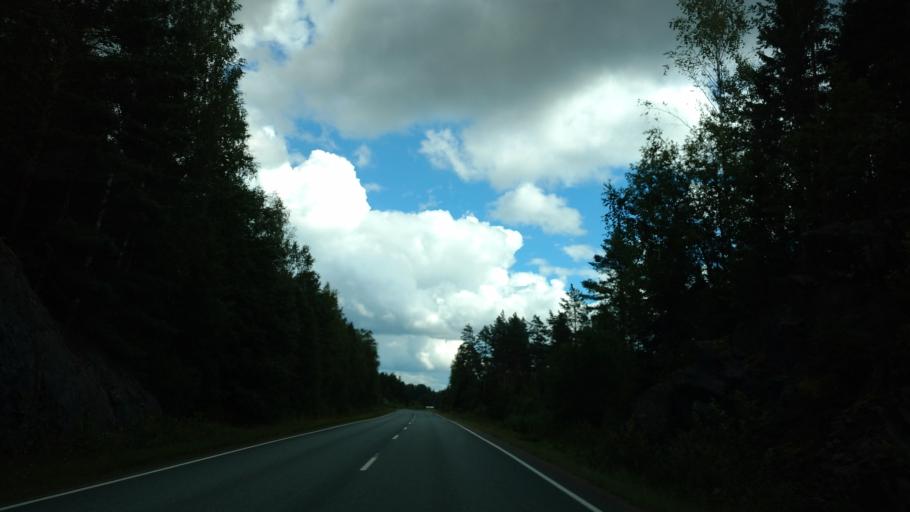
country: FI
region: Varsinais-Suomi
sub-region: Salo
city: Kisko
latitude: 60.2449
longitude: 23.5292
